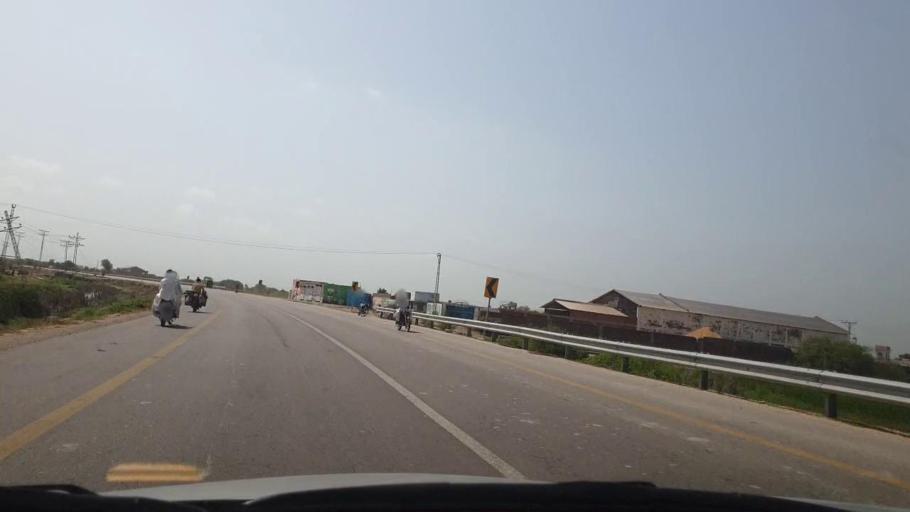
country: PK
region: Sindh
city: Matli
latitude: 25.0038
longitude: 68.6501
